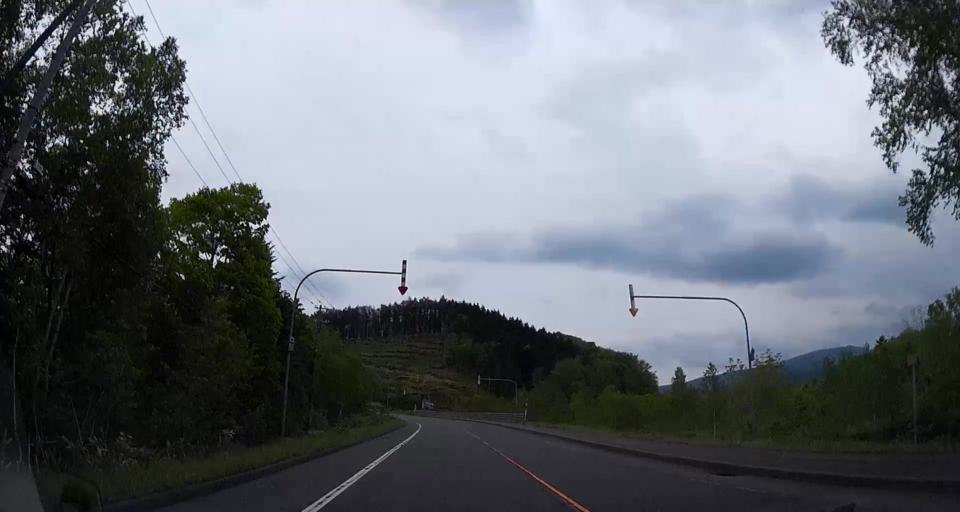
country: JP
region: Hokkaido
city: Shiraoi
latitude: 42.6784
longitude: 141.0938
